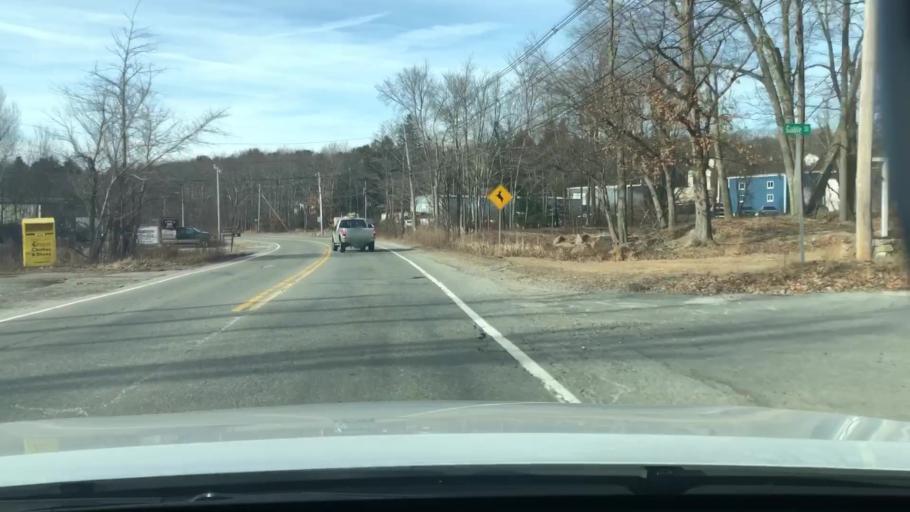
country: US
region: Massachusetts
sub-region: Worcester County
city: Upton
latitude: 42.1622
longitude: -71.5848
